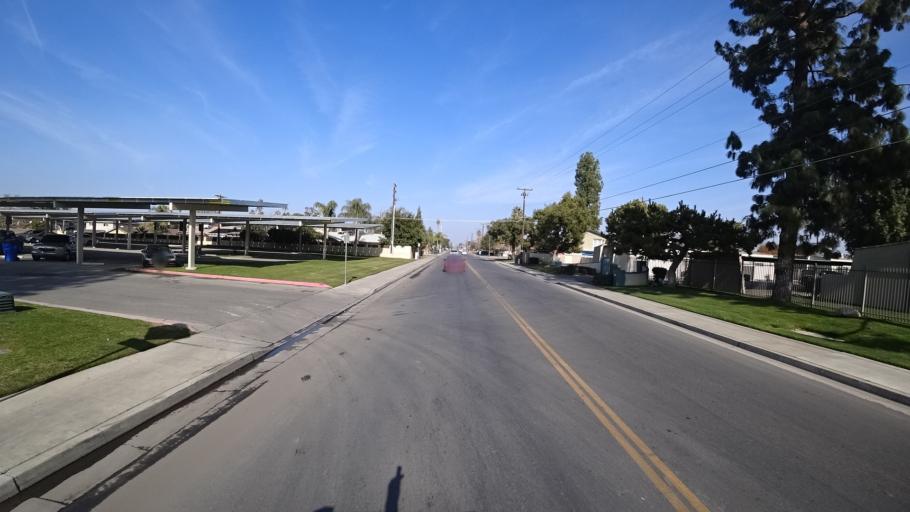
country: US
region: California
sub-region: Kern County
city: Bakersfield
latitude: 35.3355
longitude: -119.0434
